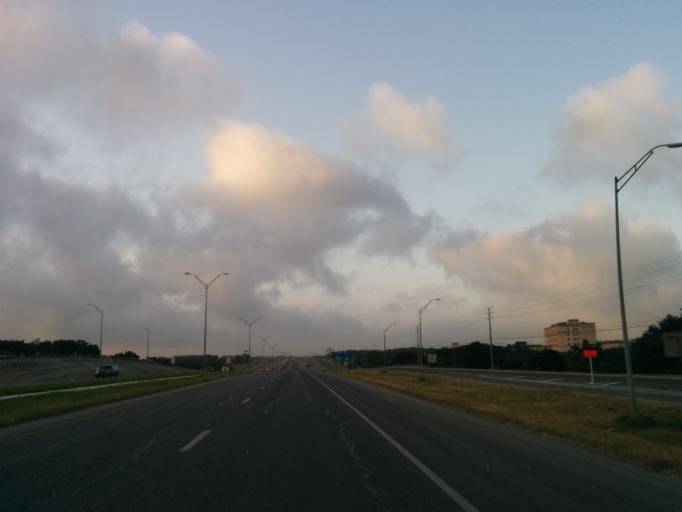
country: US
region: Texas
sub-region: Bexar County
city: Leon Valley
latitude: 29.4727
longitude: -98.6969
